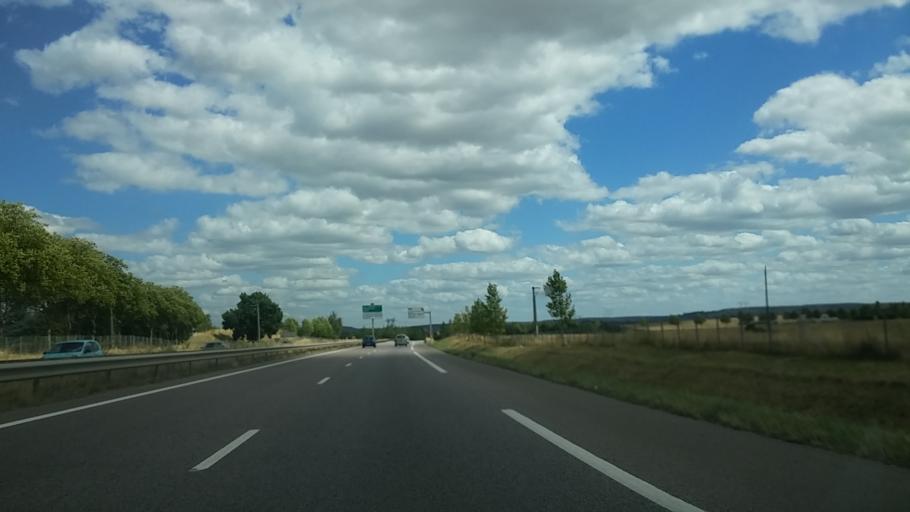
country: FR
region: Ile-de-France
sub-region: Departement des Yvelines
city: Galluis
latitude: 48.8015
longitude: 1.8074
